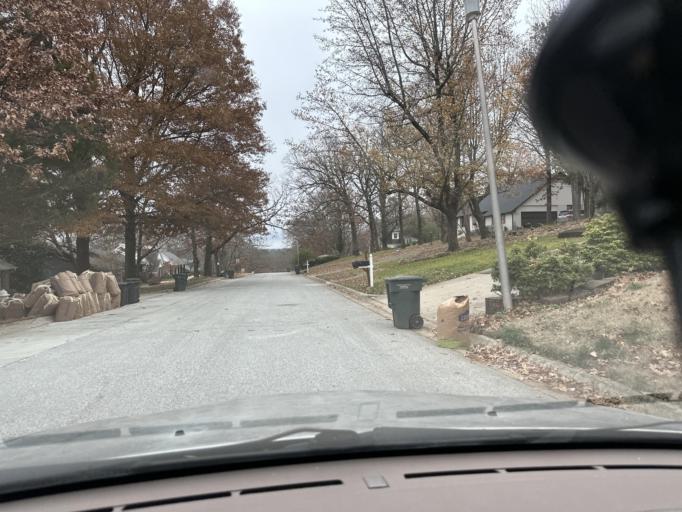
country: US
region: Arkansas
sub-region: Washington County
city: Johnson
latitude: 36.1031
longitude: -94.1440
